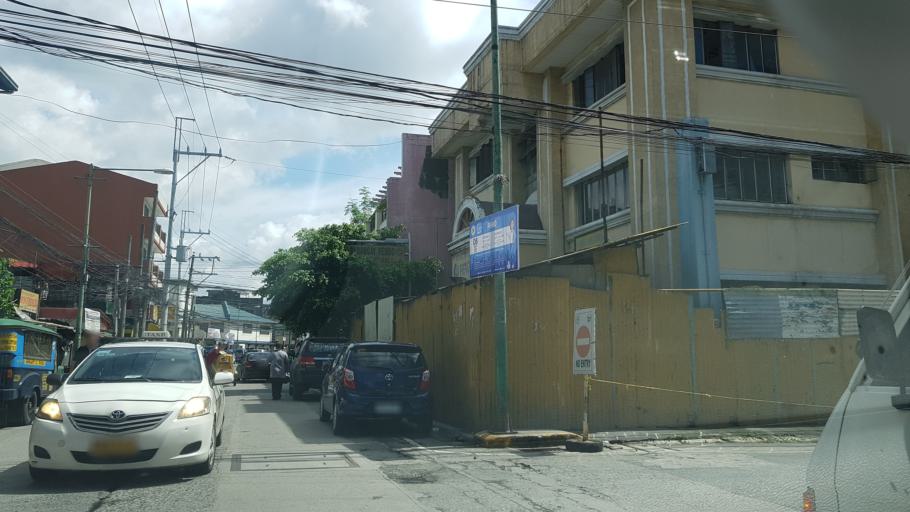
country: PH
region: Calabarzon
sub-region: Province of Rizal
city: Pateros
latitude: 14.5466
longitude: 121.0616
